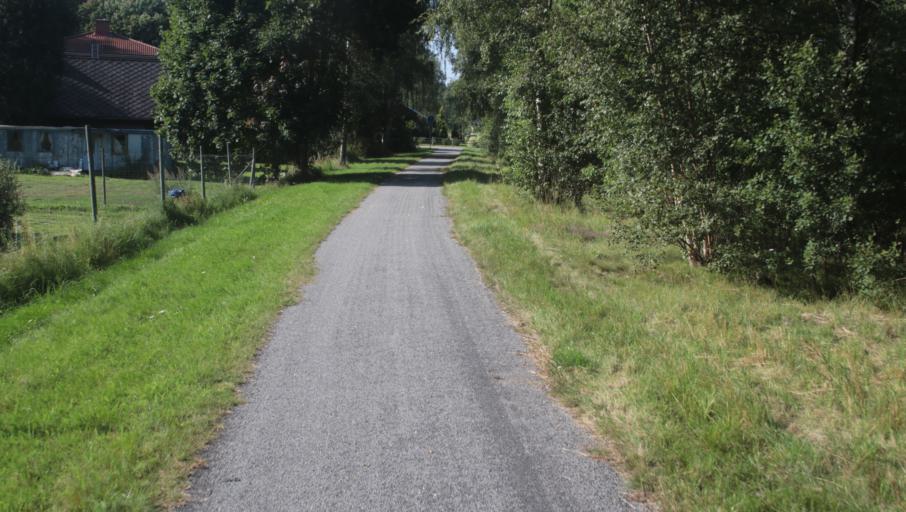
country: SE
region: Blekinge
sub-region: Karlshamns Kommun
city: Svangsta
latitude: 56.3258
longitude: 14.7034
